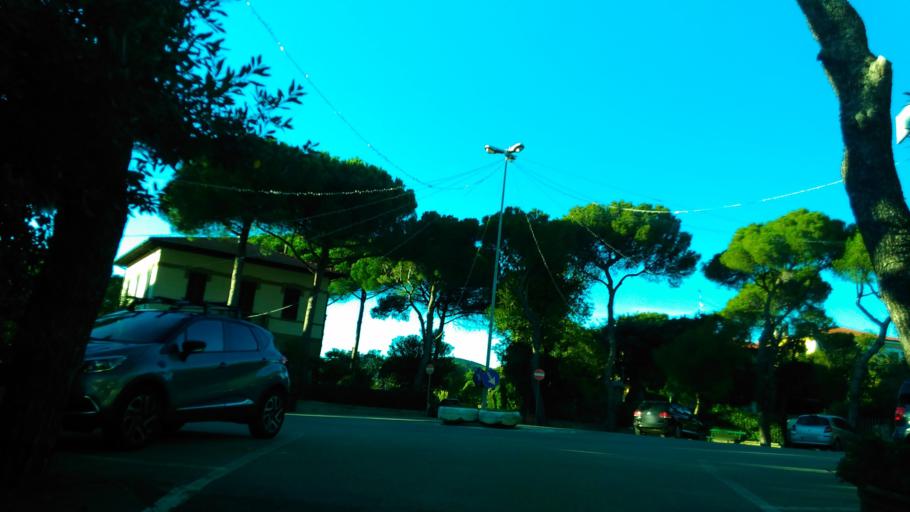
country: IT
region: Tuscany
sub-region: Provincia di Livorno
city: Quercianella
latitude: 43.4573
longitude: 10.3685
